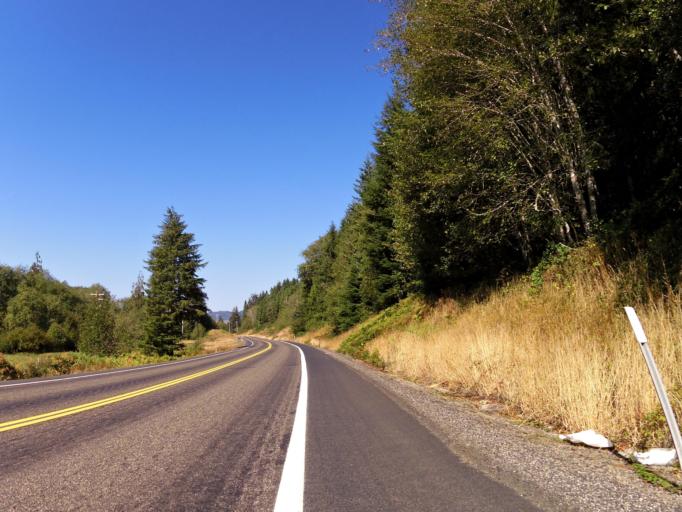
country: US
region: Oregon
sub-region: Tillamook County
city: Tillamook
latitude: 45.3256
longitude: -123.8505
